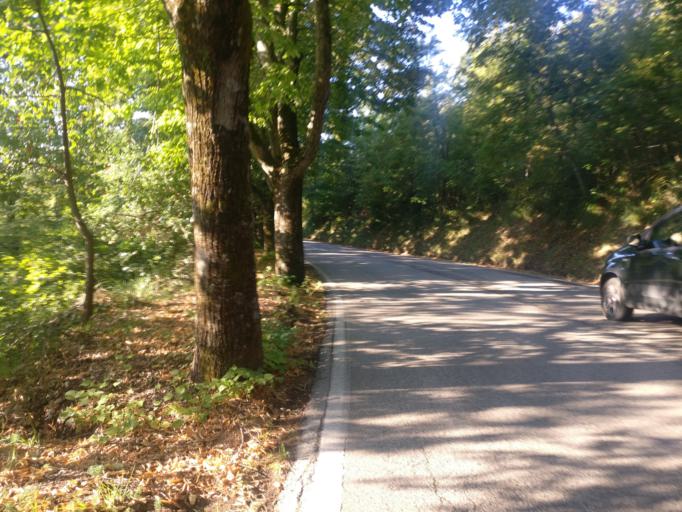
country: IT
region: The Marches
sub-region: Provincia di Ascoli Piceno
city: Montedinove
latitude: 42.9797
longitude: 13.5960
